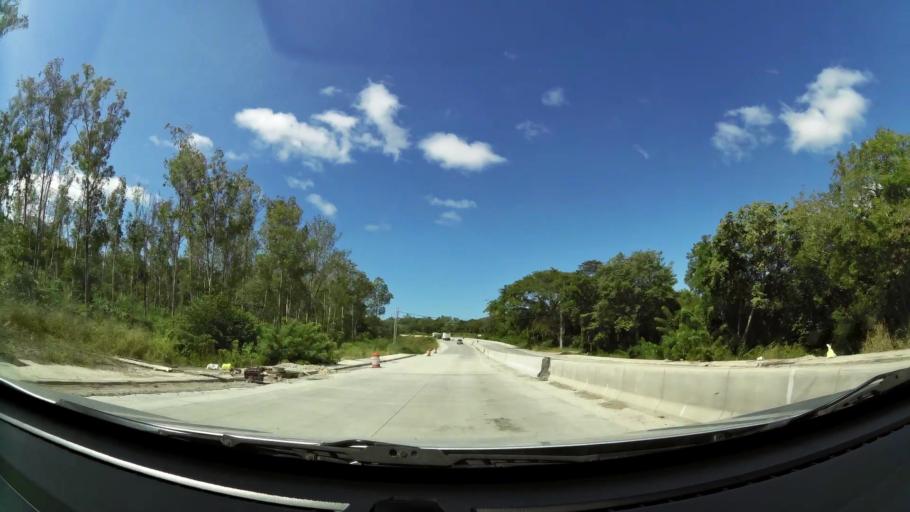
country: CR
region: Guanacaste
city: Bagaces
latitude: 10.5340
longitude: -85.2880
